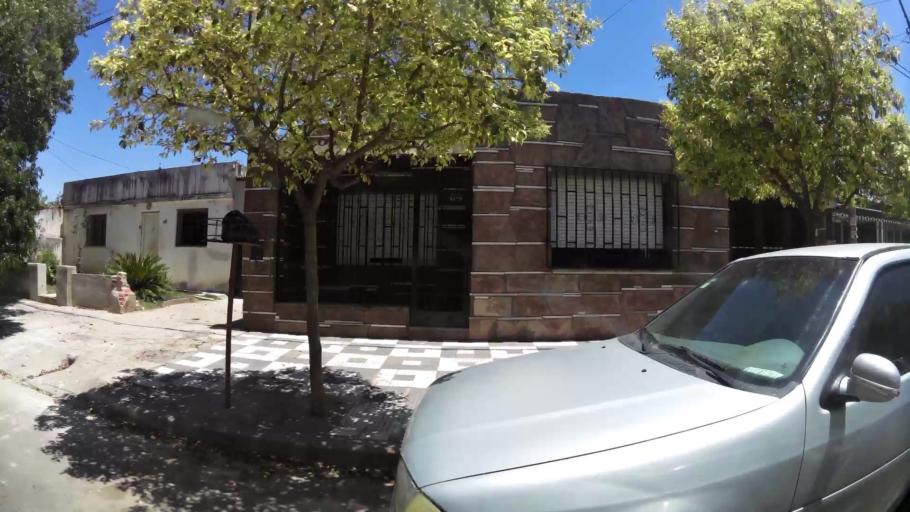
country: AR
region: Cordoba
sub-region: Departamento de Capital
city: Cordoba
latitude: -31.3837
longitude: -64.1304
